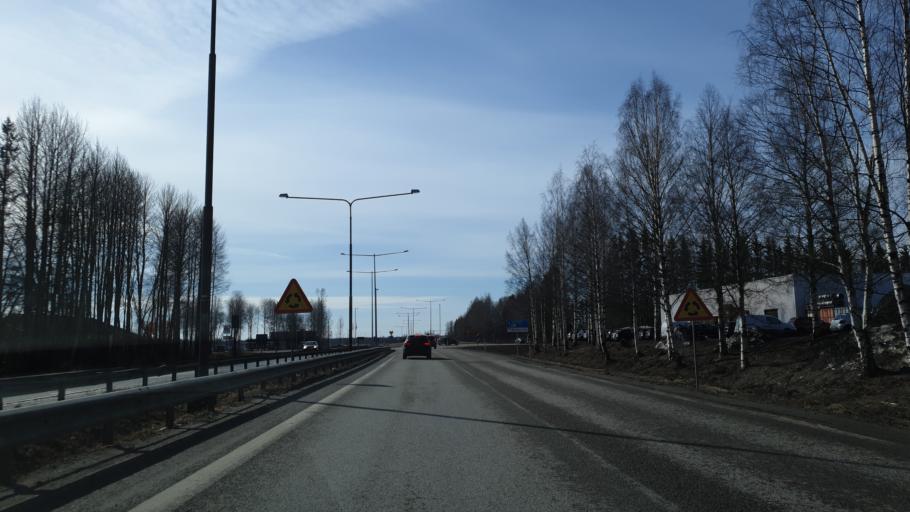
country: SE
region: Vaesterbotten
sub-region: Umea Kommun
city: Umea
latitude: 63.8132
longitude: 20.2493
